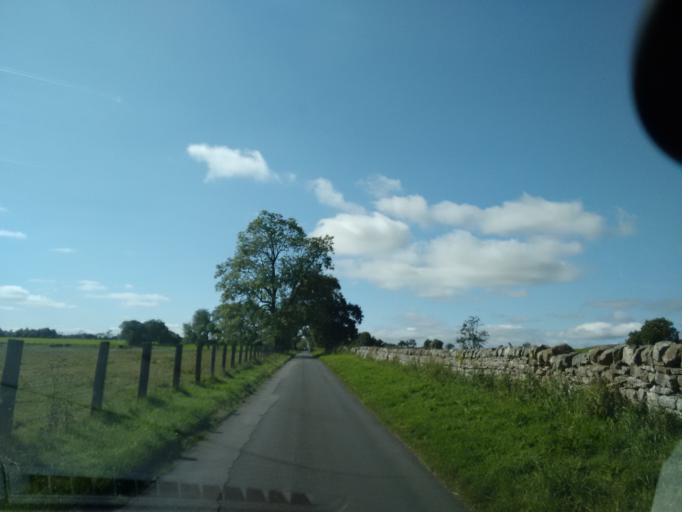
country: GB
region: England
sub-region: Northumberland
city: Bardon Mill
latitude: 54.9912
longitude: -2.3683
